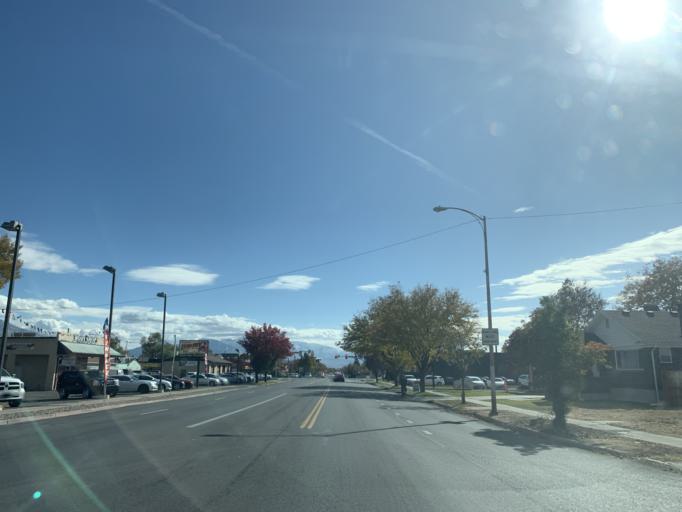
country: US
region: Utah
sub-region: Utah County
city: Provo
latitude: 40.2310
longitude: -111.6623
